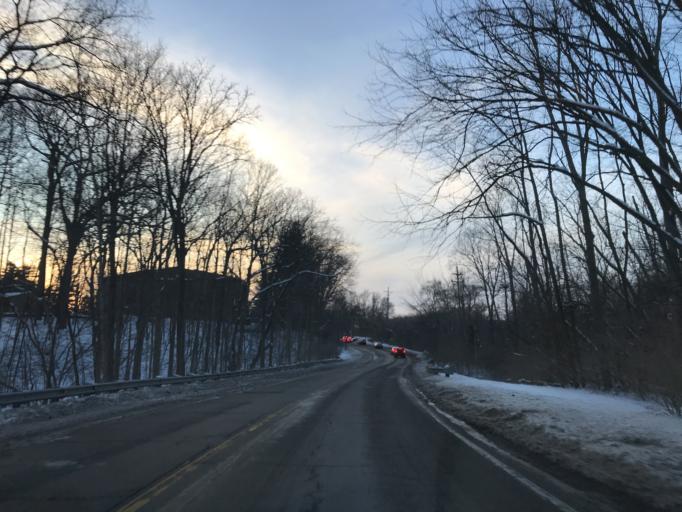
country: US
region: Michigan
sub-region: Oakland County
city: Farmington
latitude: 42.4563
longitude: -83.3142
